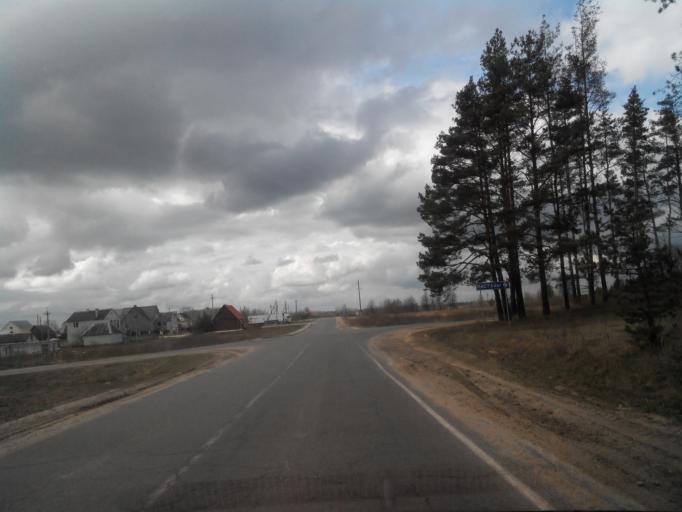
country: BY
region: Vitebsk
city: Pastavy
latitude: 55.0953
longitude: 26.8421
